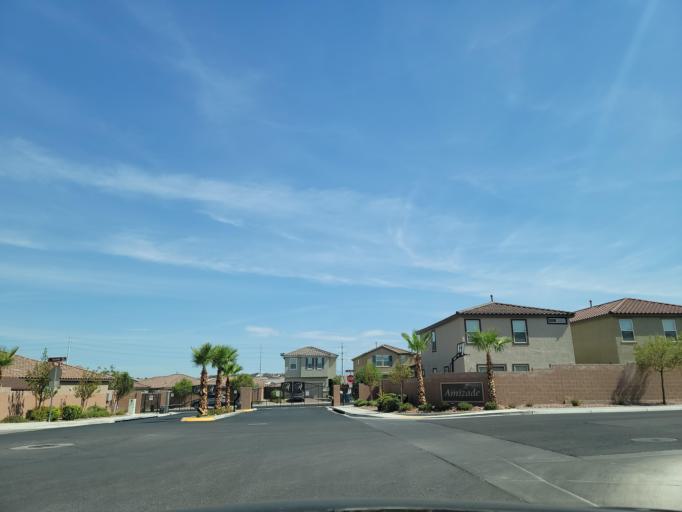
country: US
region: Nevada
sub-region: Clark County
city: Spring Valley
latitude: 36.0812
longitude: -115.2838
